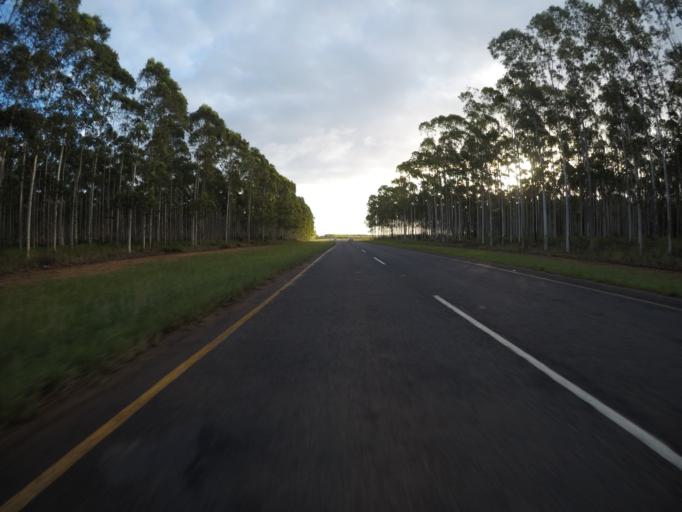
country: ZA
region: KwaZulu-Natal
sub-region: uMkhanyakude District Municipality
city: Mtubatuba
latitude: -28.4076
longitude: 32.1992
